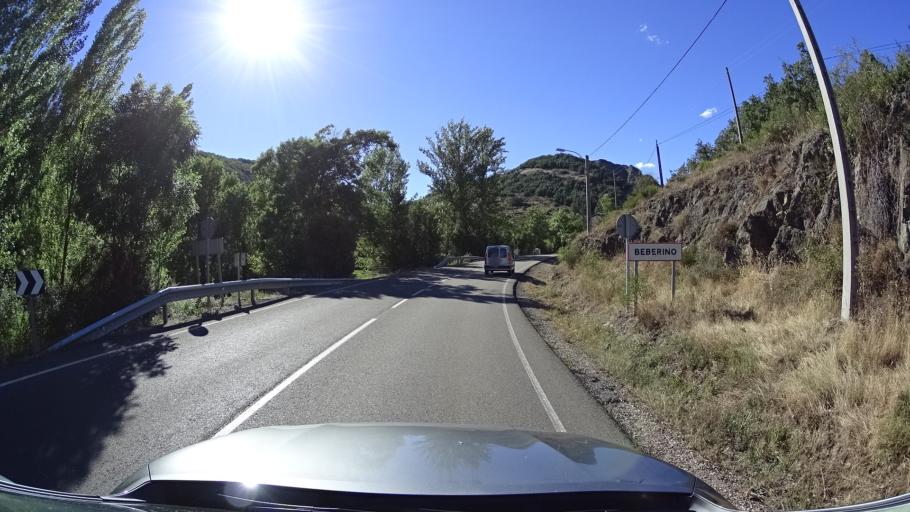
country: ES
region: Castille and Leon
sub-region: Provincia de Leon
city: La Pola de Gordon
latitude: 42.8629
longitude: -5.6787
